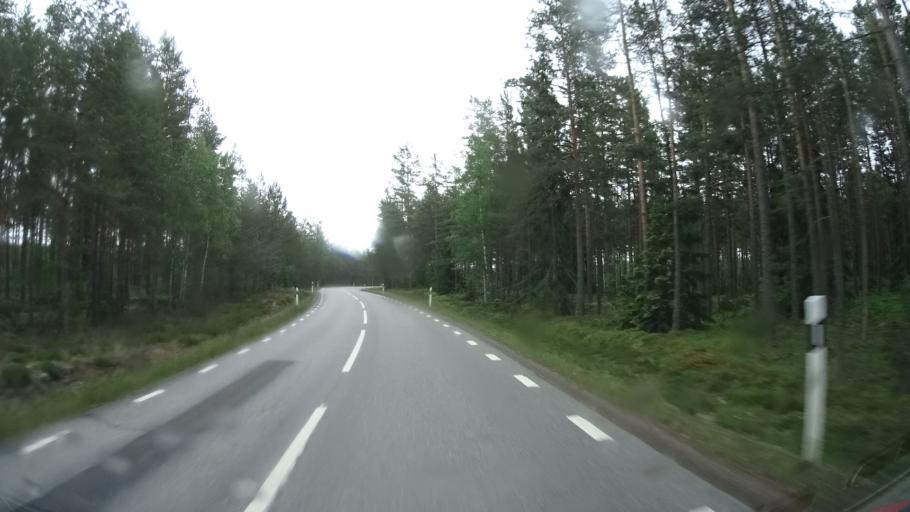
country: SE
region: Kalmar
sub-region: Hultsfreds Kommun
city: Hultsfred
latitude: 57.5279
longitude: 15.7887
